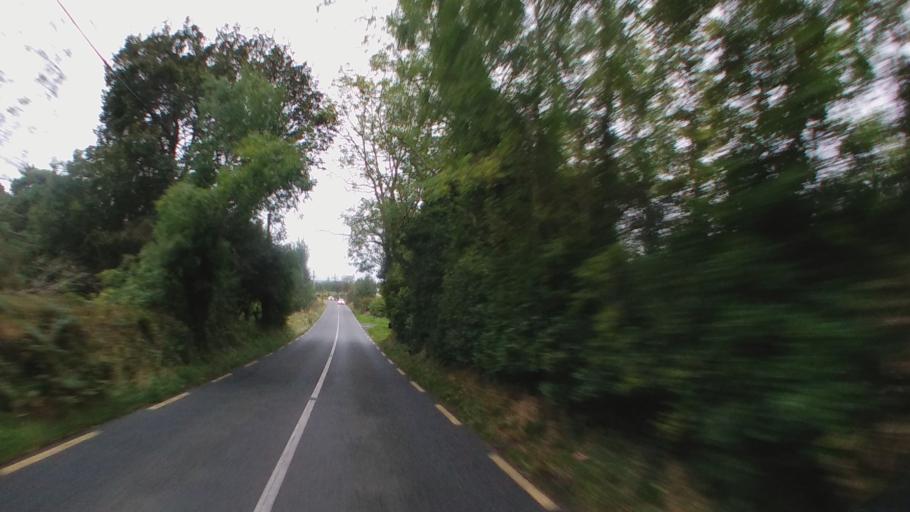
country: IE
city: Newtownmountkennedy
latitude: 53.0966
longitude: -6.2029
